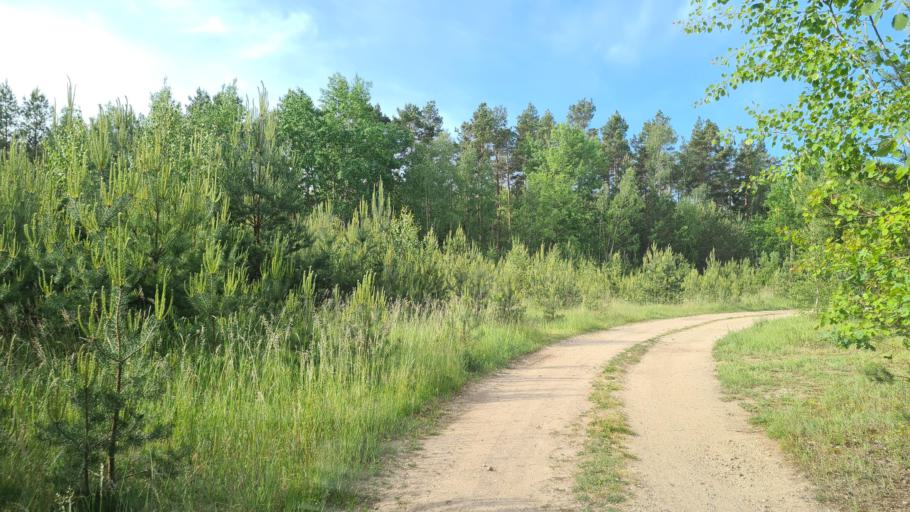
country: DE
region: Brandenburg
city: Sallgast
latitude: 51.5929
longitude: 13.7970
